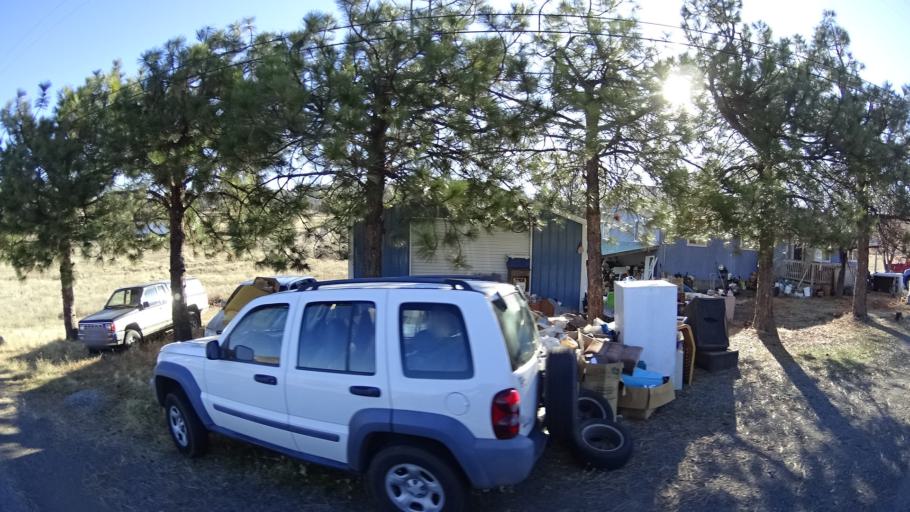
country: US
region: California
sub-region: Siskiyou County
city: Montague
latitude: 41.8902
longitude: -122.4915
